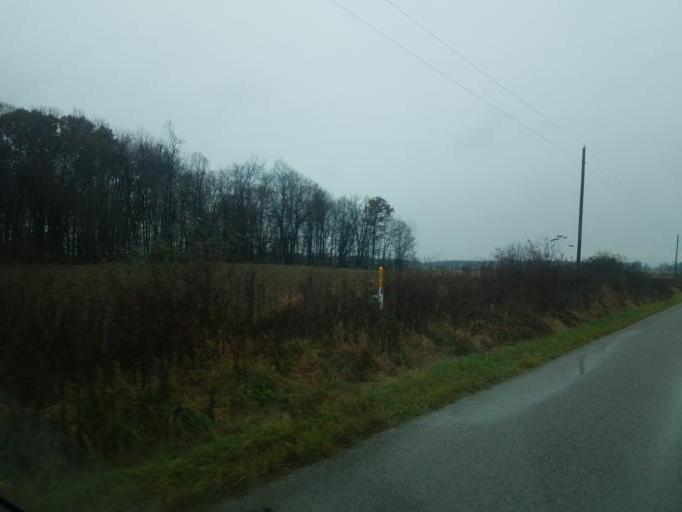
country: US
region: Ohio
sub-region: Knox County
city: Centerburg
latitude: 40.3724
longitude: -82.6661
